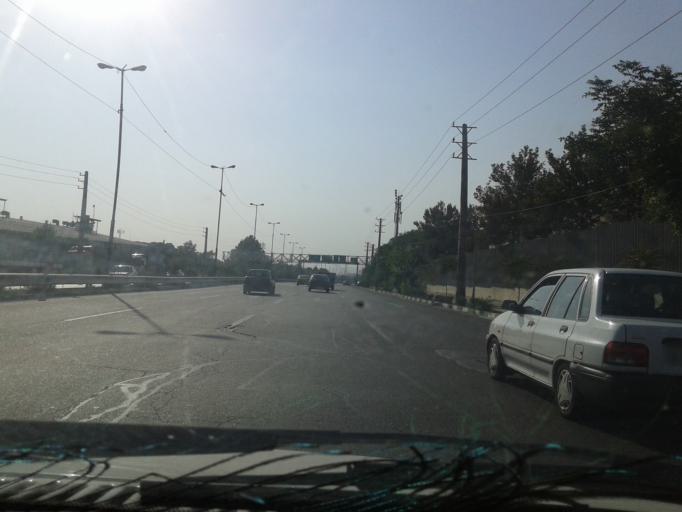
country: IR
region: Tehran
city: Tehran
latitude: 35.7242
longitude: 51.5731
